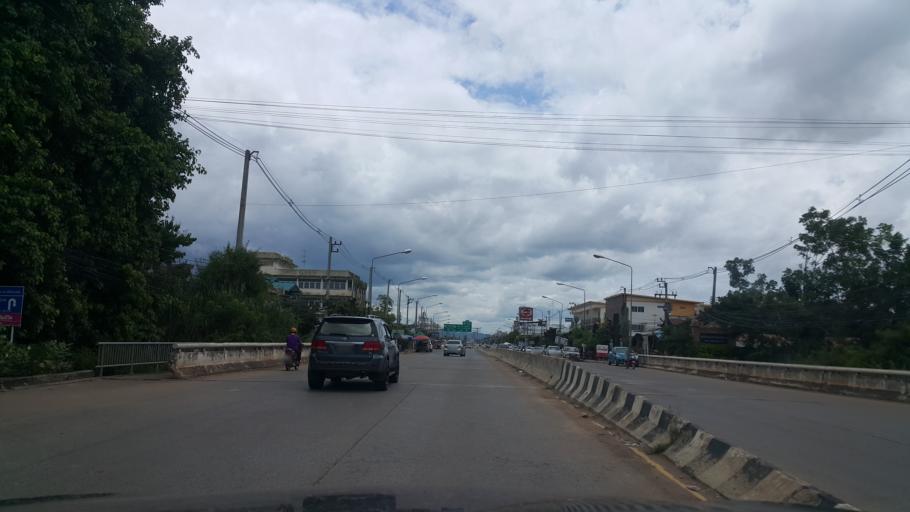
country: TH
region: Sukhothai
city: Sukhothai
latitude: 17.0088
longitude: 99.8099
